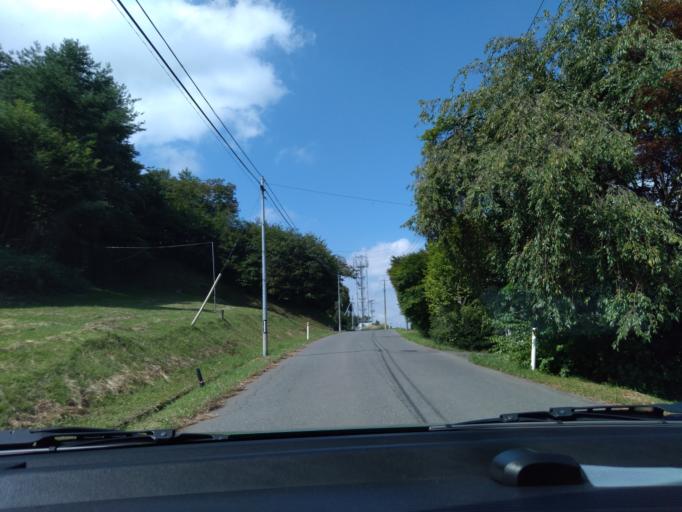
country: JP
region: Iwate
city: Shizukuishi
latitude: 39.6699
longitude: 140.9689
